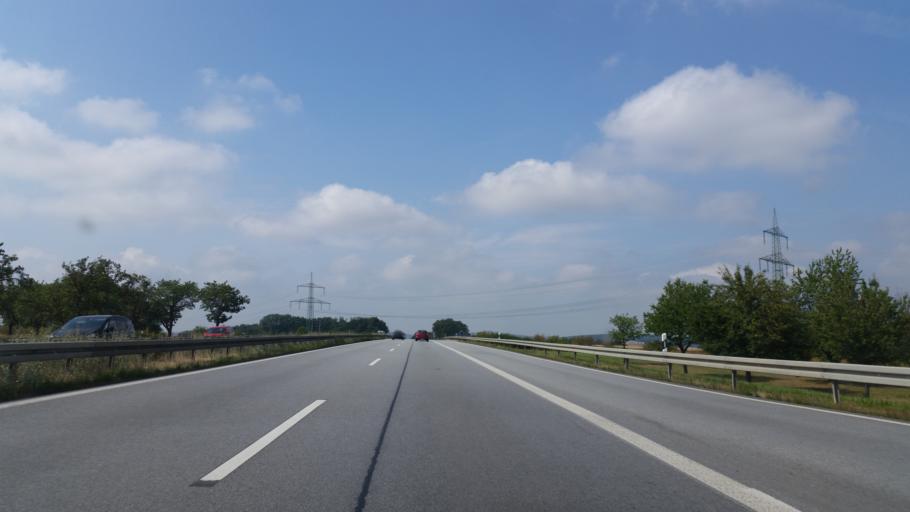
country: DE
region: Saxony
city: Panschwitz-Kuckau
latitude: 51.1983
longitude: 14.2226
